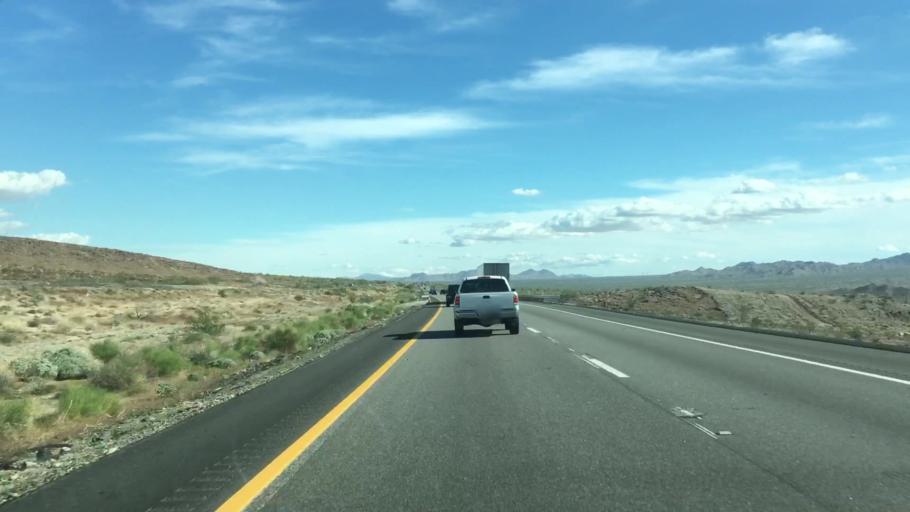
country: US
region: California
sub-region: Riverside County
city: Mecca
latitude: 33.6653
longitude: -115.8882
